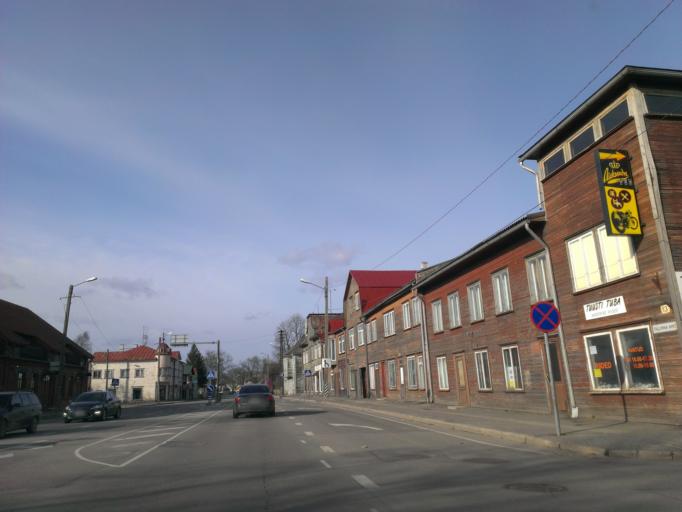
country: EE
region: Paernumaa
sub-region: Paernu linn
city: Parnu
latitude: 58.3921
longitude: 24.4952
